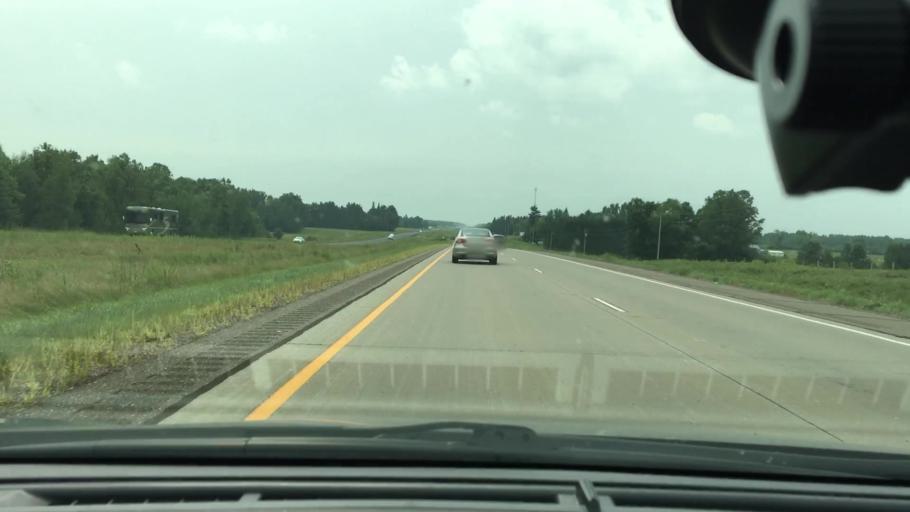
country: US
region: Minnesota
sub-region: Mille Lacs County
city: Milaca
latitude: 45.9611
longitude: -93.6625
